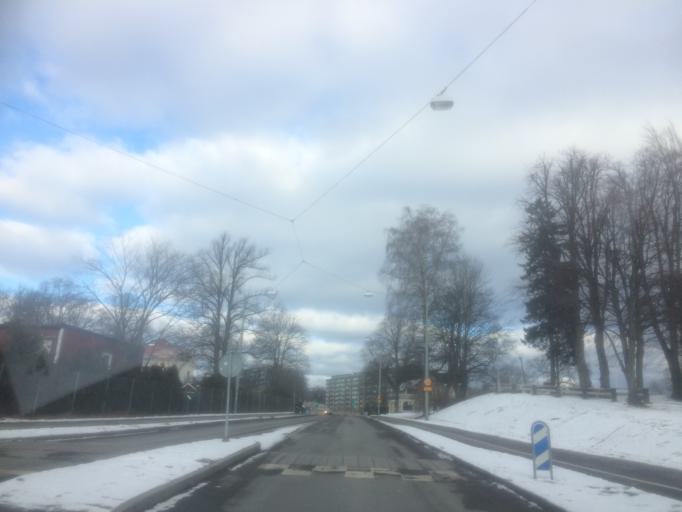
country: SE
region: Vaestra Goetaland
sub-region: Goteborg
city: Goeteborg
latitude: 57.7028
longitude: 12.0039
